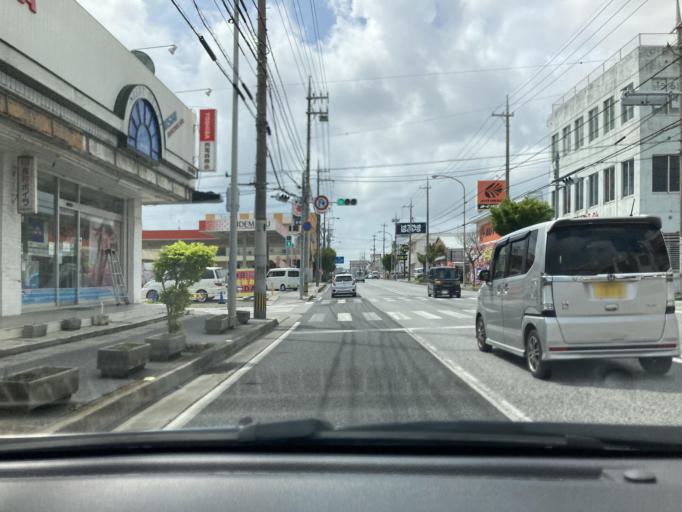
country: JP
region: Okinawa
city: Okinawa
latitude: 26.3538
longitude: 127.8296
